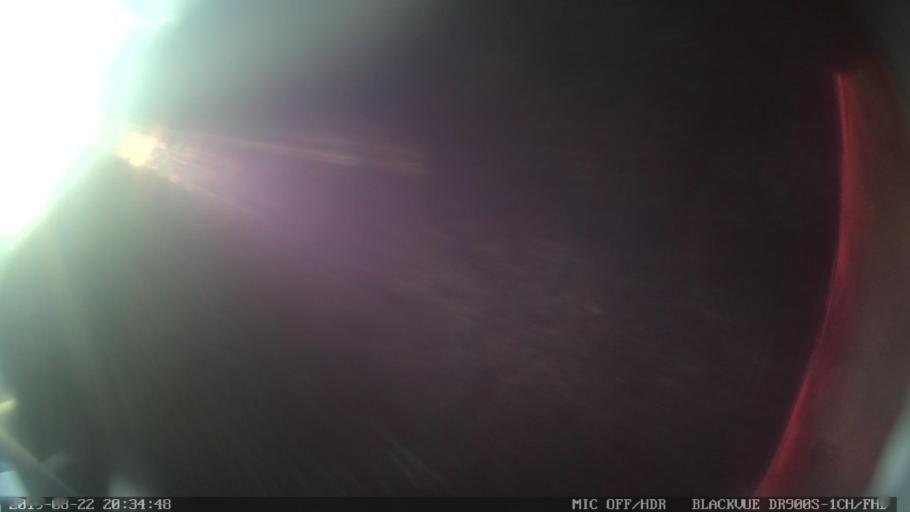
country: PT
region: Portalegre
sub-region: Nisa
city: Nisa
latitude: 39.6981
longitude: -7.6958
